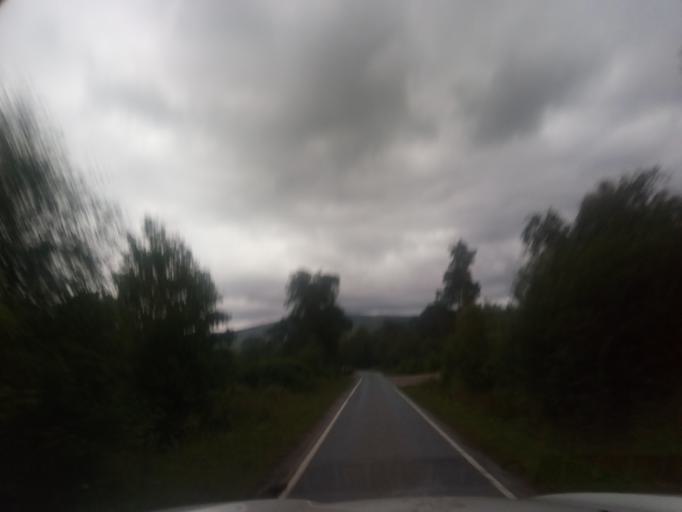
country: GB
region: Scotland
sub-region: Highland
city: Fort William
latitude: 56.8531
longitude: -5.3297
